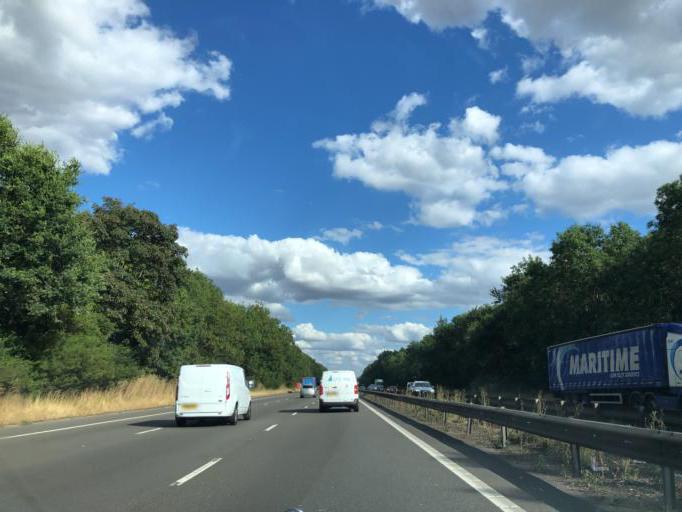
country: GB
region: England
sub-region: Milton Keynes
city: Stoke Goldington
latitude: 52.1109
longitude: -0.7892
